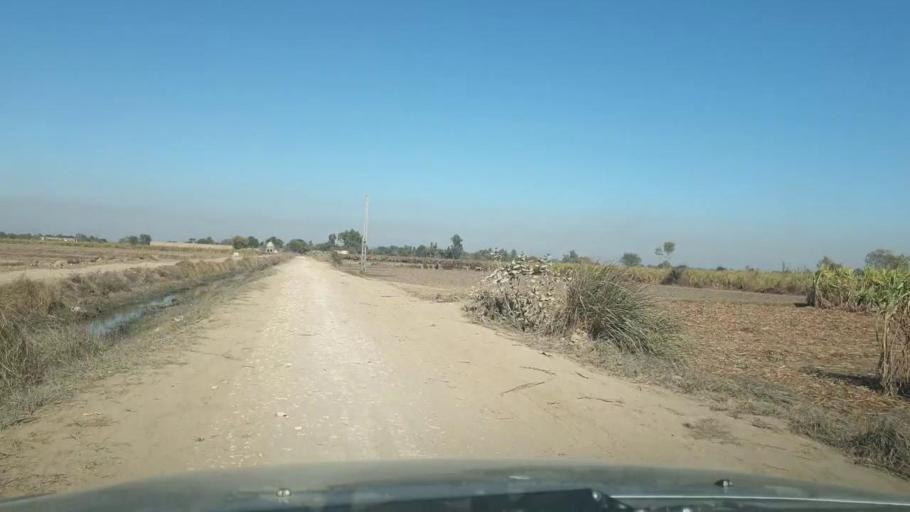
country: PK
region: Sindh
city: Ghotki
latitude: 28.0384
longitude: 69.2466
